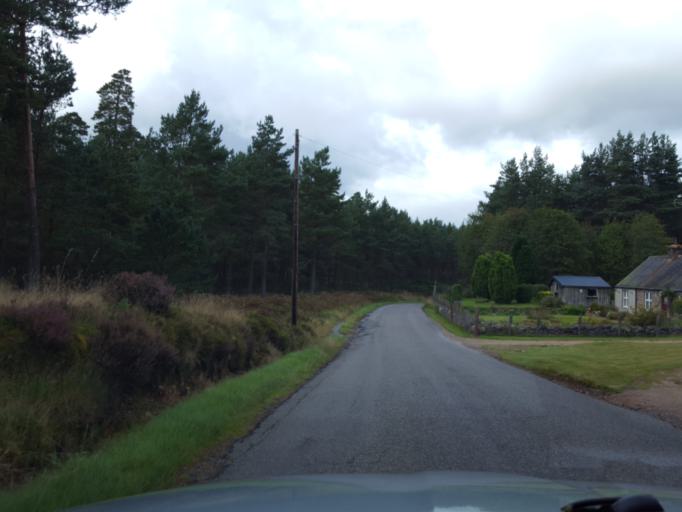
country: GB
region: Scotland
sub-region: Aberdeenshire
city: Banchory
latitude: 57.0034
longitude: -2.5834
